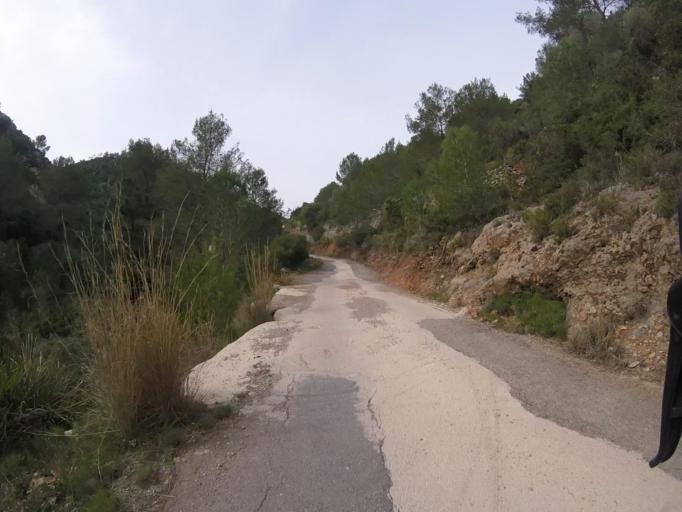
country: ES
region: Valencia
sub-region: Provincia de Castello
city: Cabanes
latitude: 40.1112
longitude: 0.0436
